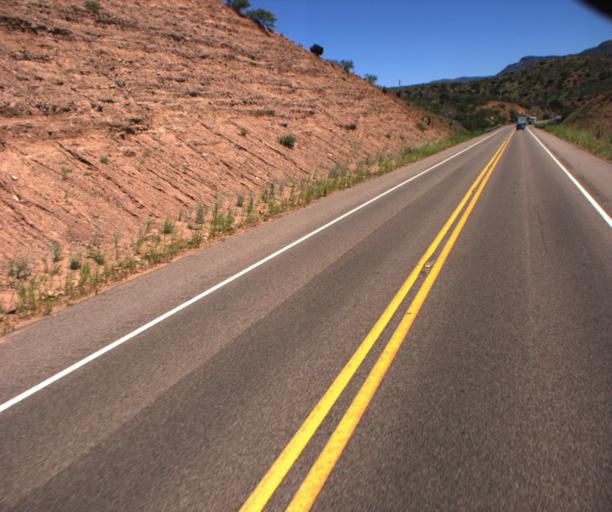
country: US
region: Arizona
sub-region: Gila County
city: Globe
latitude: 33.5841
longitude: -110.6509
